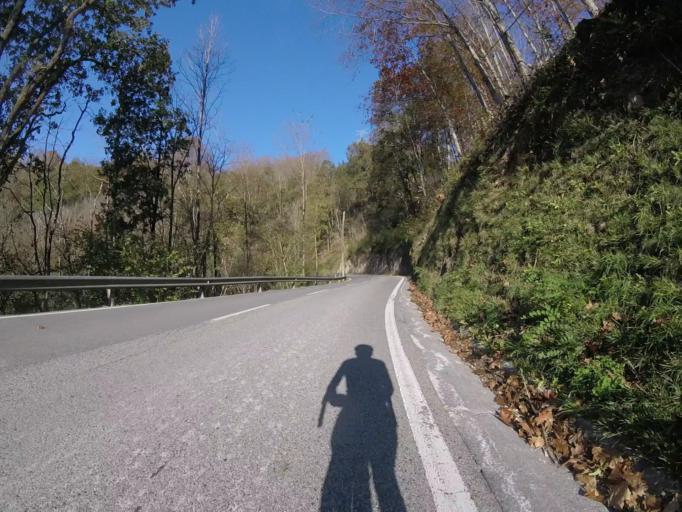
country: ES
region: Navarre
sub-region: Provincia de Navarra
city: Igantzi
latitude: 43.2263
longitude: -1.6878
